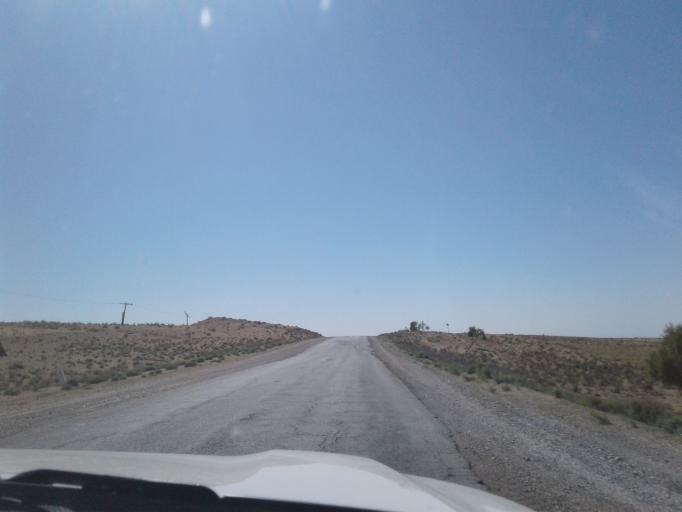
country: AF
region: Badghis
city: Bala Murghab
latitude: 35.9595
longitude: 62.7629
